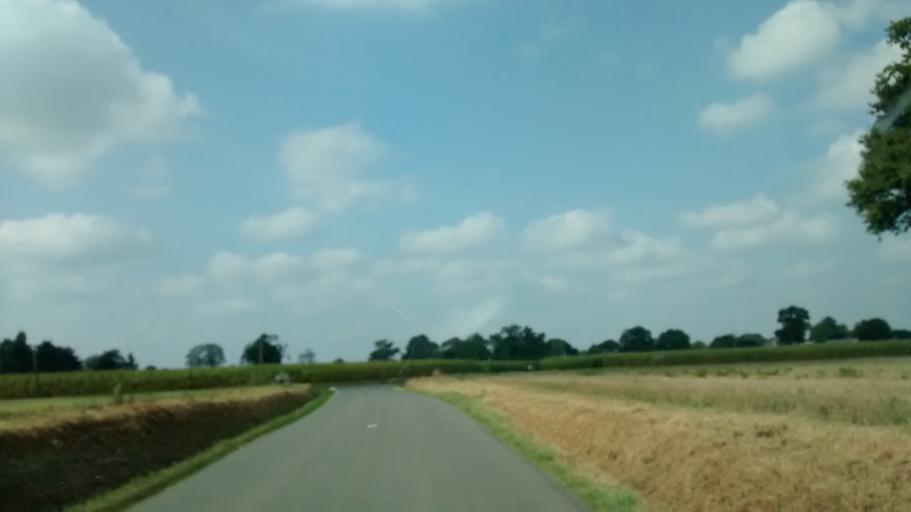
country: FR
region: Brittany
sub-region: Departement d'Ille-et-Vilaine
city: Livre-sur-Changeon
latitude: 48.2291
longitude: -1.2809
